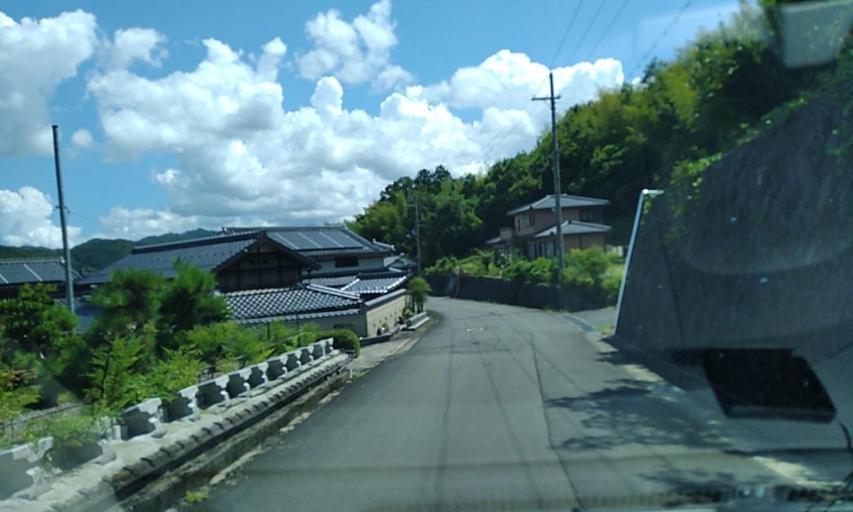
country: JP
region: Kyoto
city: Ayabe
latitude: 35.3539
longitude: 135.2348
